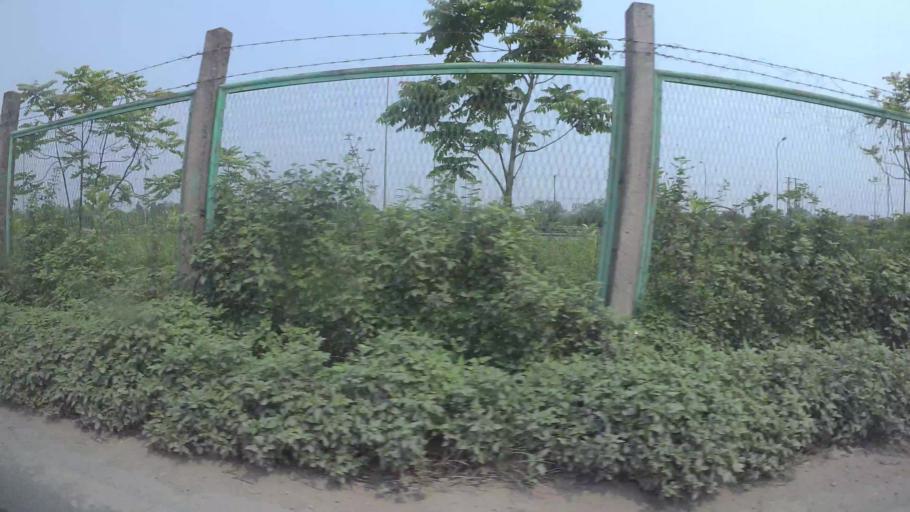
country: VN
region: Ha Noi
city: Quoc Oai
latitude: 21.0050
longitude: 105.6903
